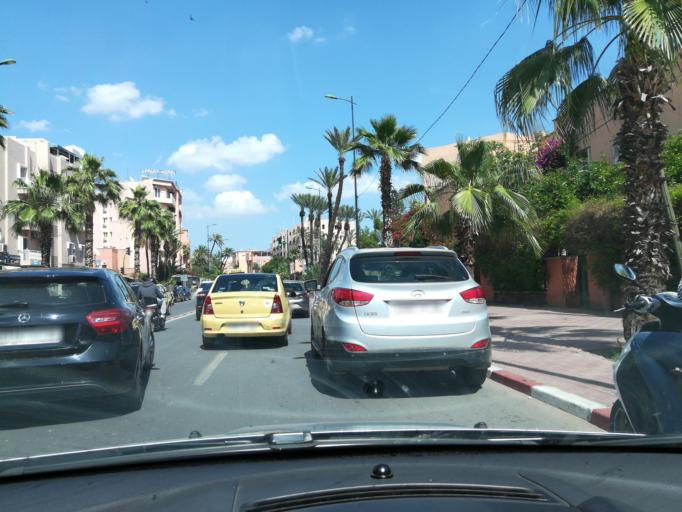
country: MA
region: Marrakech-Tensift-Al Haouz
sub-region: Marrakech
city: Marrakesh
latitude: 31.6377
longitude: -8.0098
